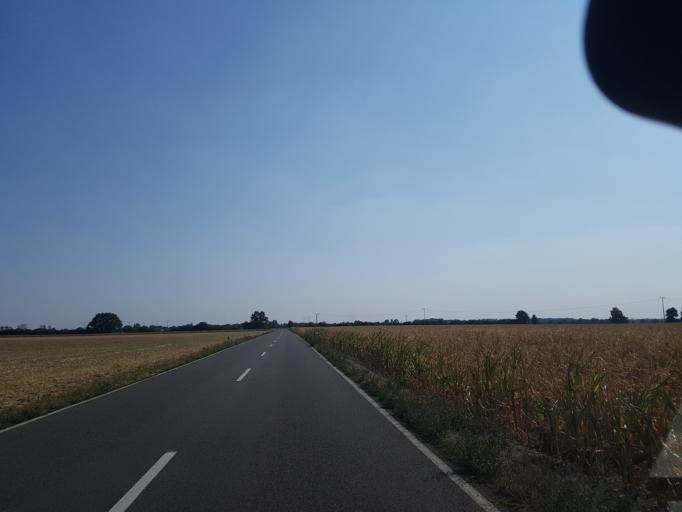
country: DE
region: Saxony-Anhalt
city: Annaburg
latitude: 51.6887
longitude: 12.9974
